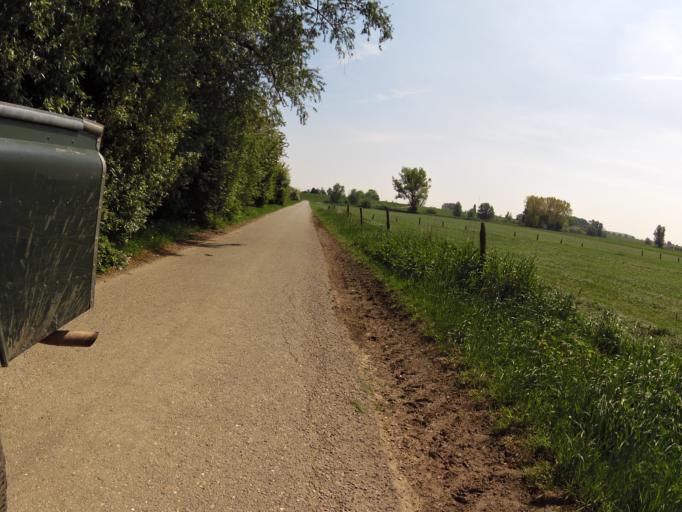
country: NL
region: Gelderland
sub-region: Gemeente Neerijnen
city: Neerijnen
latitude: 51.8118
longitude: 5.3044
